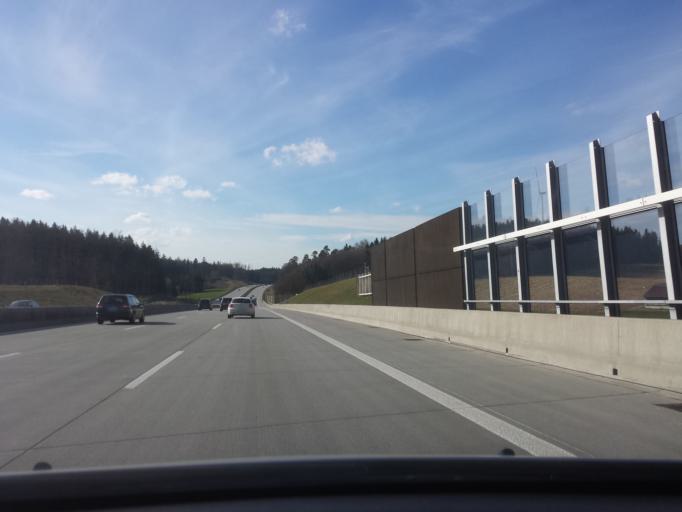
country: DE
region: Bavaria
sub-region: Upper Bavaria
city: Odelzhausen
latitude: 48.3228
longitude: 11.1812
